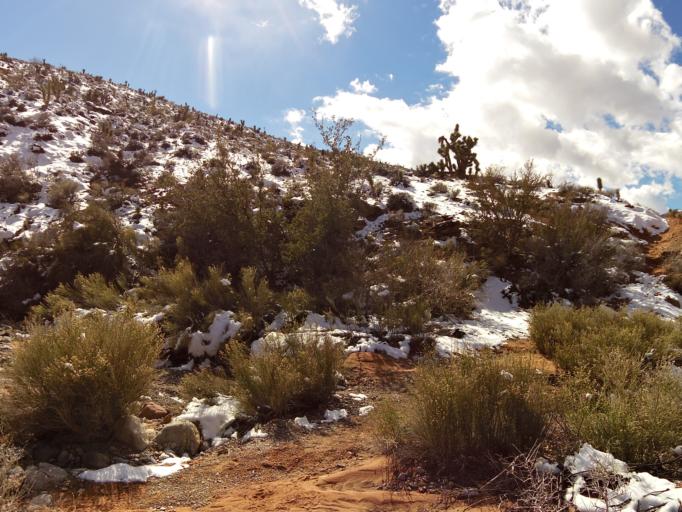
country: US
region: Nevada
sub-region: Clark County
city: Summerlin South
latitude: 36.1413
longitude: -115.4203
